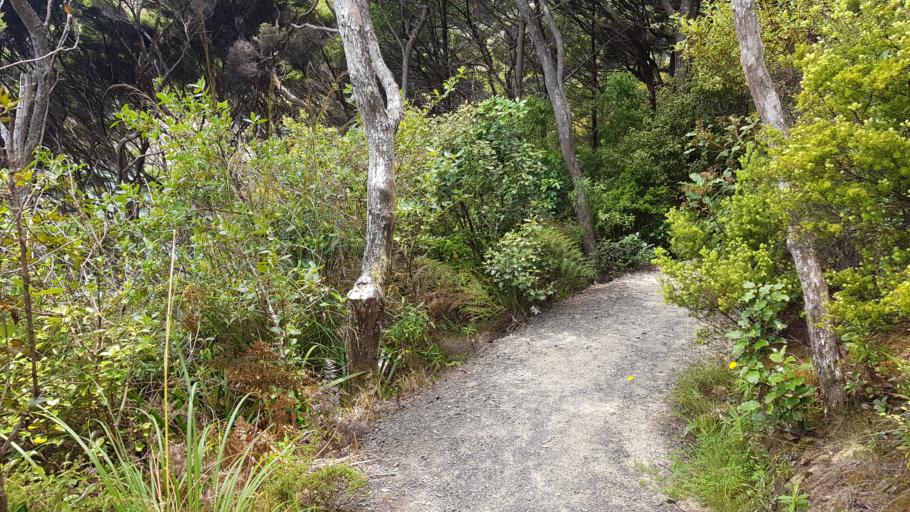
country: NZ
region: Auckland
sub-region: Auckland
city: North Shore
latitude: -36.8242
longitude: 174.7094
